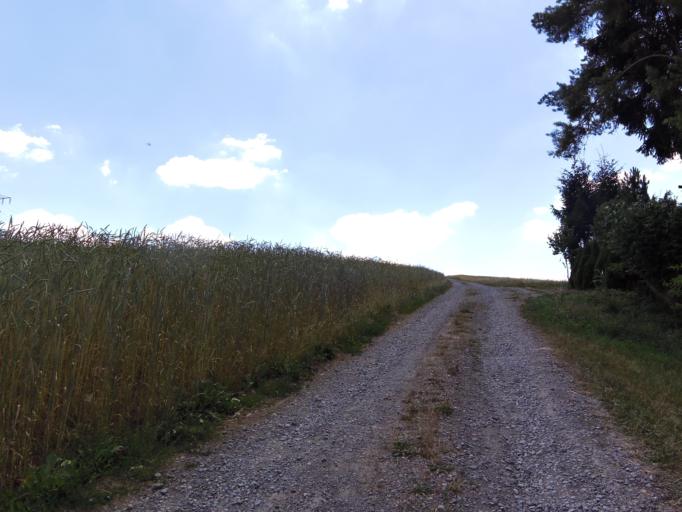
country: DE
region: Bavaria
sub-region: Regierungsbezirk Unterfranken
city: Gadheim
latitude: 49.8310
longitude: 9.9283
